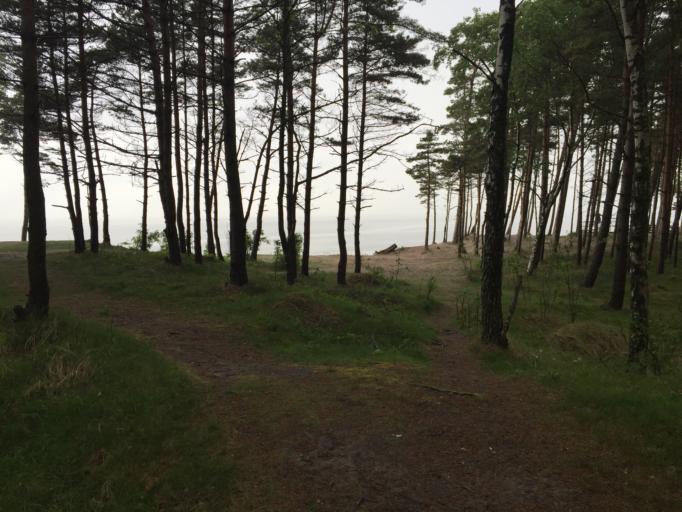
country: LT
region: Klaipedos apskritis
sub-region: Klaipeda
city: Klaipeda
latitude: 55.7978
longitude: 21.0680
